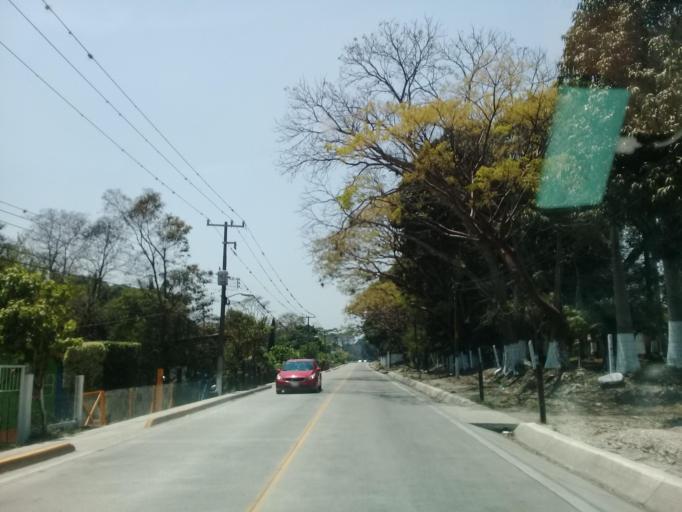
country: MX
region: Veracruz
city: Paraje Nuevo
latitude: 18.8729
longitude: -96.8704
